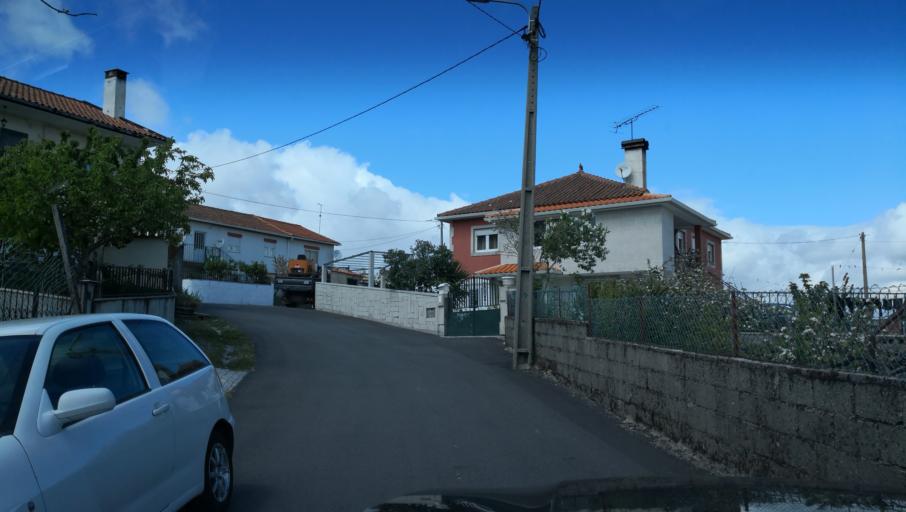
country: PT
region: Vila Real
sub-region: Vila Real
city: Vila Real
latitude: 41.4093
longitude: -7.7129
